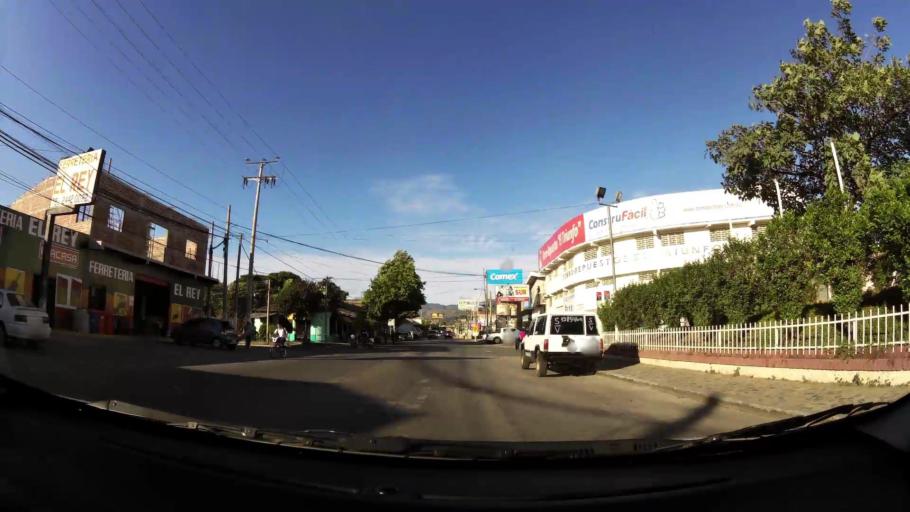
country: SV
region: Santa Ana
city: Metapan
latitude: 14.3260
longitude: -89.4435
